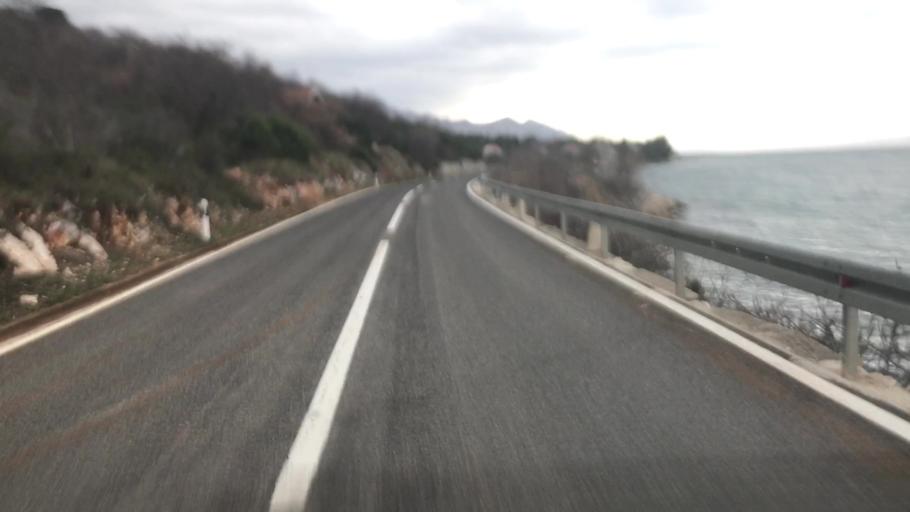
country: HR
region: Zadarska
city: Razanac
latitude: 44.3340
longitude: 15.3546
